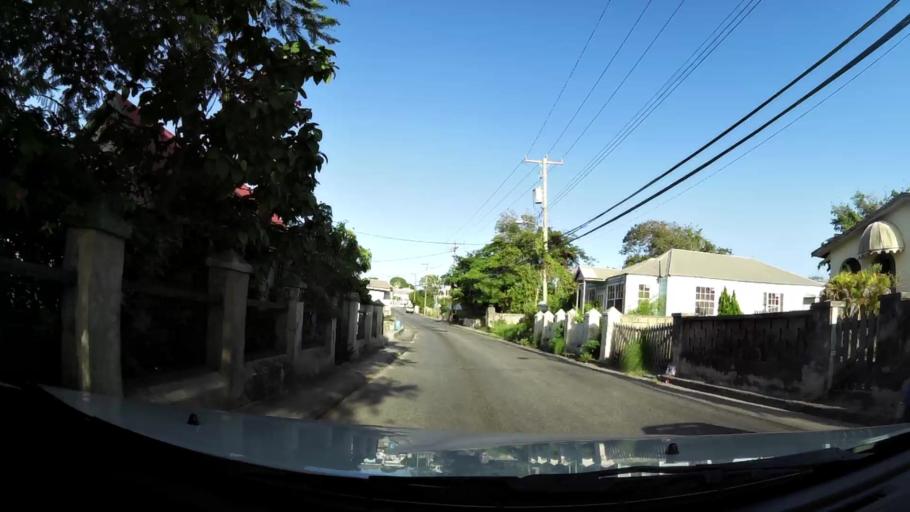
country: BB
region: Saint Michael
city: Bridgetown
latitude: 13.0772
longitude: -59.6033
